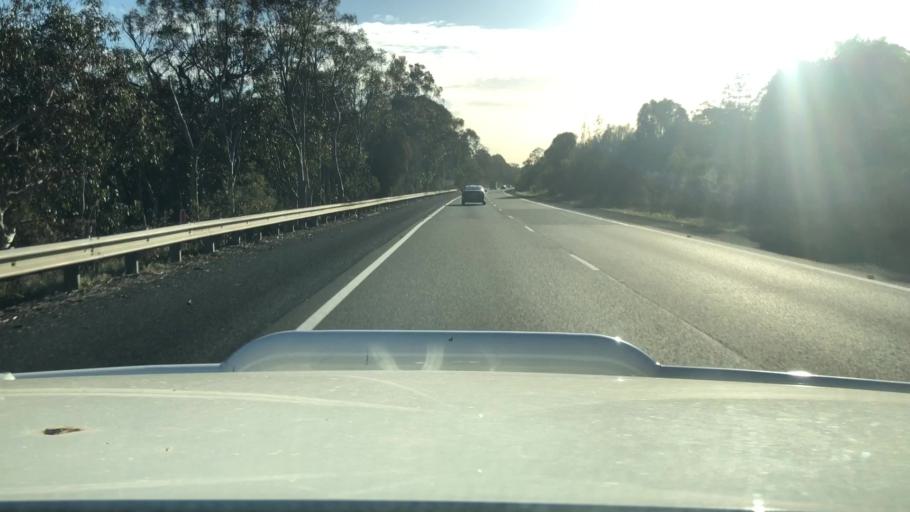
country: AU
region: New South Wales
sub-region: Wingecarribee
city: Colo Vale
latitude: -34.3791
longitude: 150.5272
